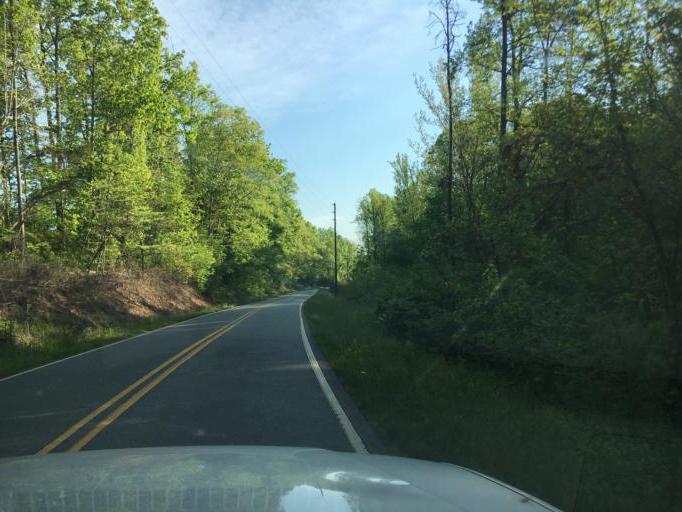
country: US
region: North Carolina
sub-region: Rutherford County
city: Rutherfordton
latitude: 35.3025
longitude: -82.0058
